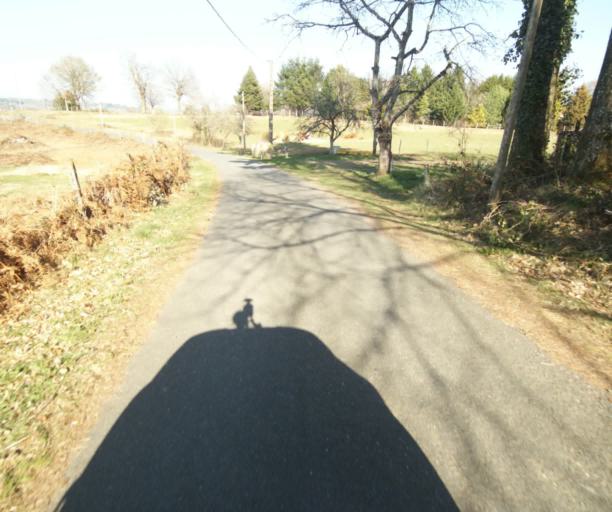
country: FR
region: Limousin
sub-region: Departement de la Correze
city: Saint-Clement
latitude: 45.3105
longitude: 1.6882
